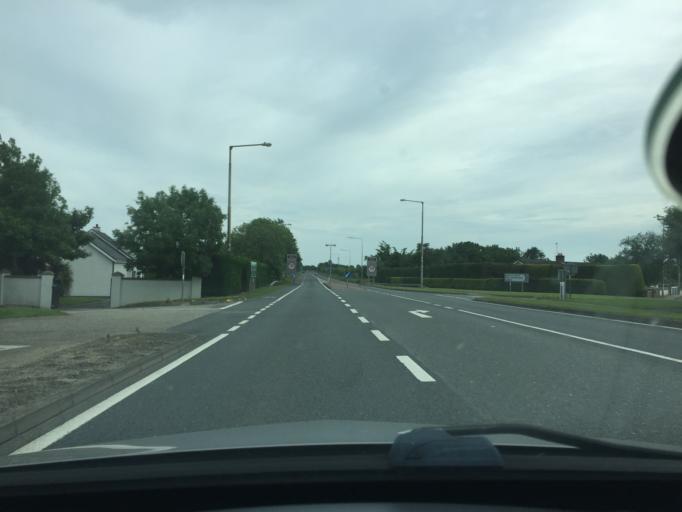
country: IE
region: Leinster
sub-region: Loch Garman
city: Enniscorthy
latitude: 52.4203
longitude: -6.5288
